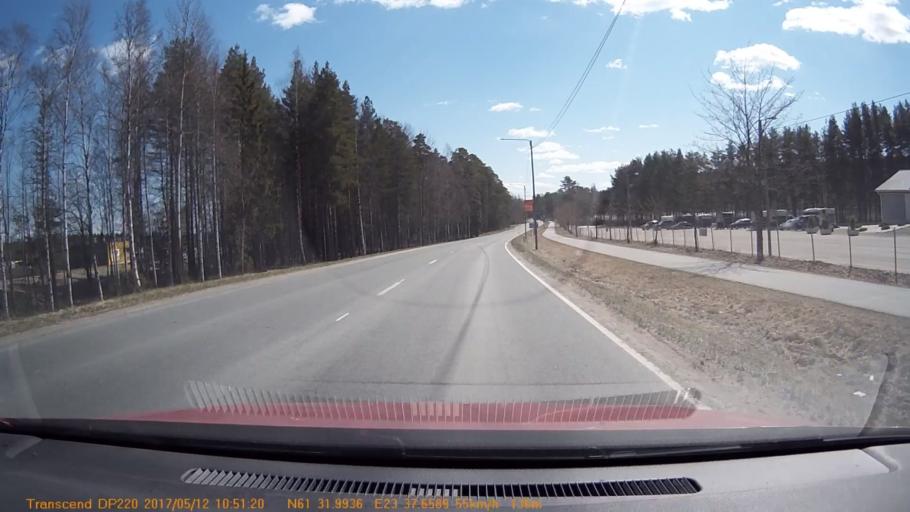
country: FI
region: Pirkanmaa
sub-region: Tampere
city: Yloejaervi
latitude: 61.5328
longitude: 23.6275
